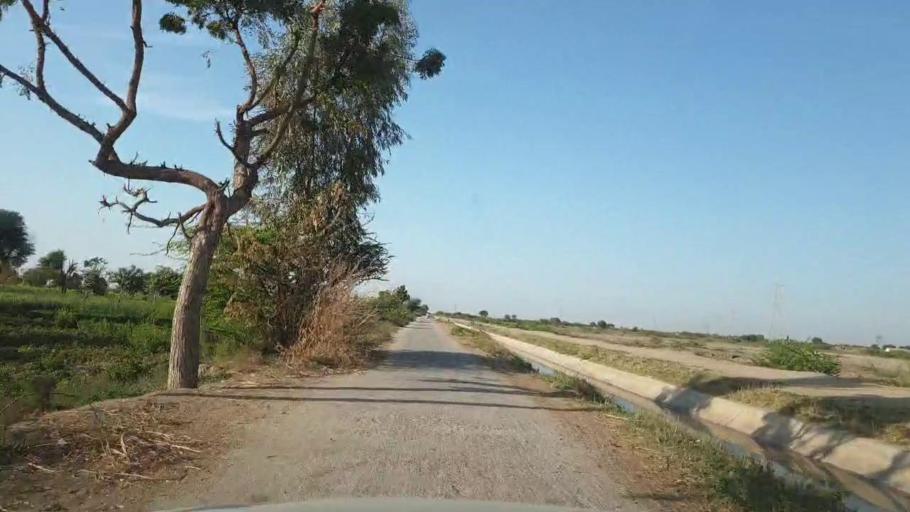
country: PK
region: Sindh
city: Kunri
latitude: 25.0887
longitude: 69.4292
